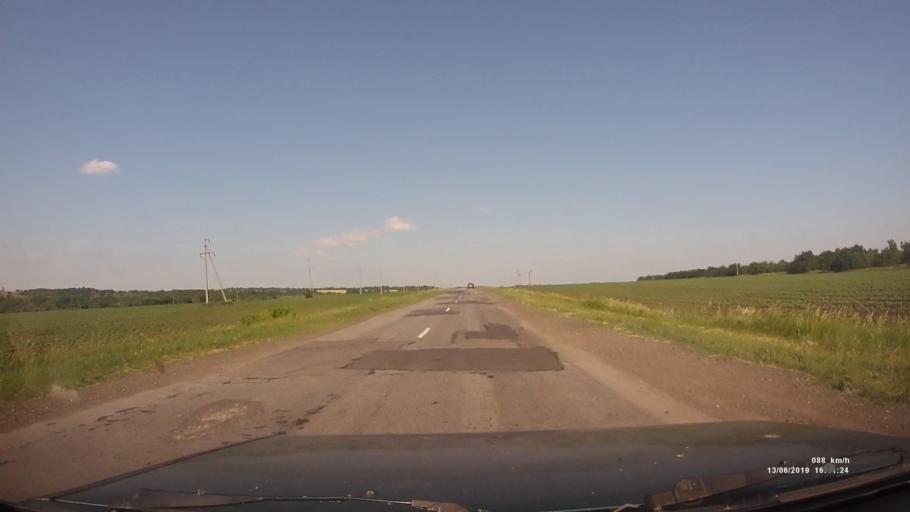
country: RU
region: Rostov
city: Kazanskaya
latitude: 49.8435
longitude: 41.2524
